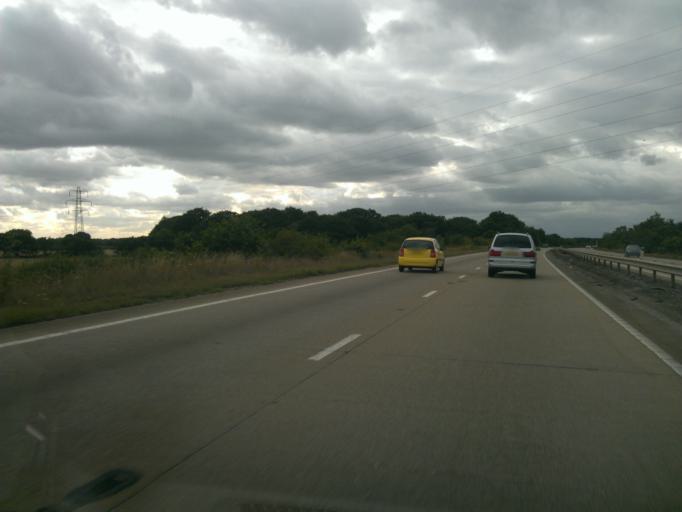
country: GB
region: England
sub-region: Essex
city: Alresford
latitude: 51.8988
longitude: 0.9868
